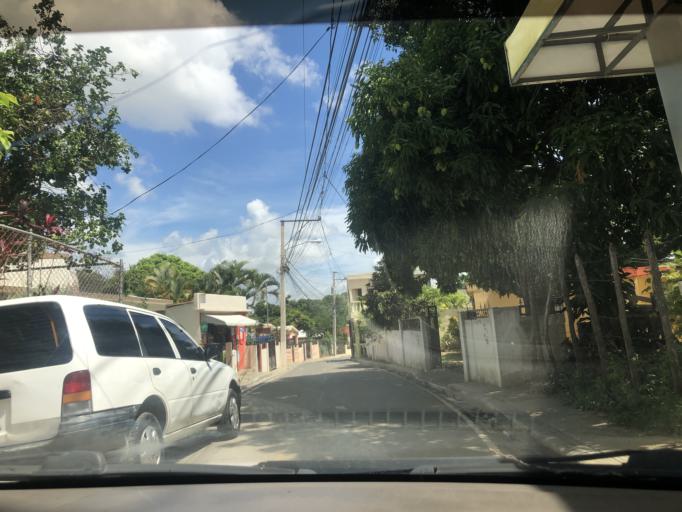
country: DO
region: Santiago
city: Santiago de los Caballeros
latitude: 19.4114
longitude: -70.7052
